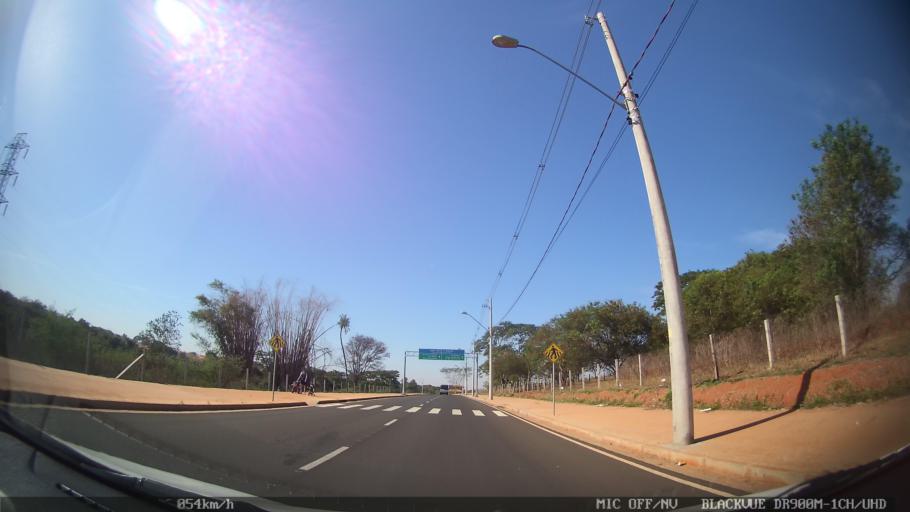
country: BR
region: Sao Paulo
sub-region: Sao Jose Do Rio Preto
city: Sao Jose do Rio Preto
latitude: -20.7622
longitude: -49.3690
